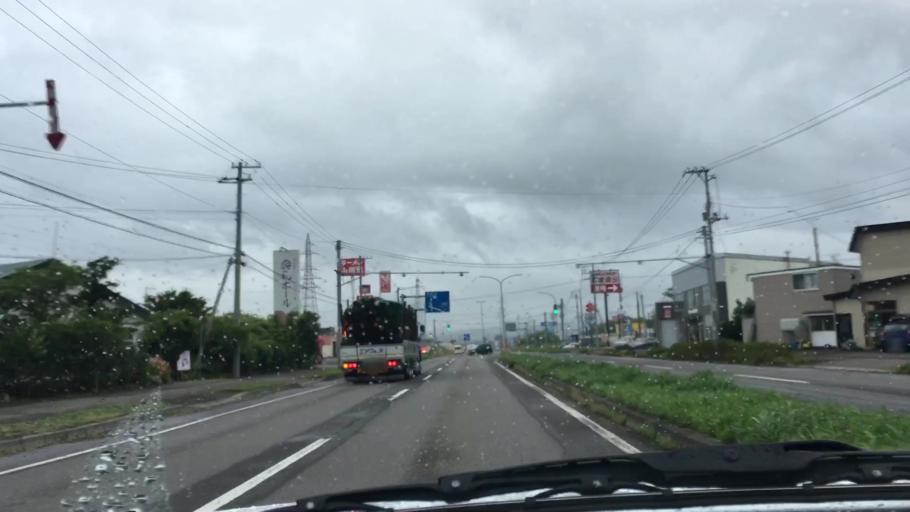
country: JP
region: Hokkaido
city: Nanae
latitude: 42.2575
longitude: 140.2792
